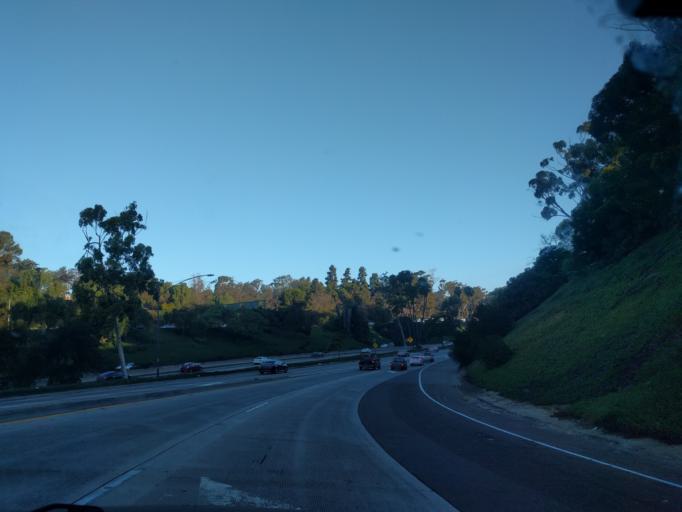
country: US
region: California
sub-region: San Diego County
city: San Diego
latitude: 32.7251
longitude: -117.1552
